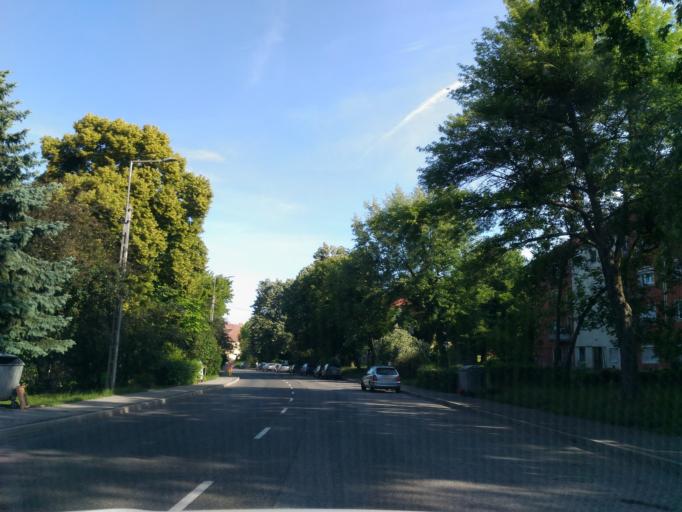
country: HU
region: Baranya
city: Komlo
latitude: 46.1830
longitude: 18.2594
